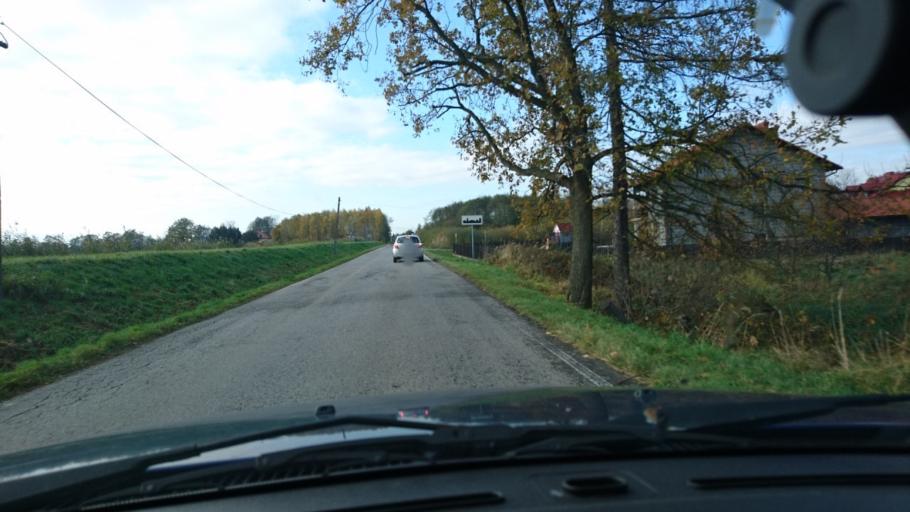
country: PL
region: Lesser Poland Voivodeship
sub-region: Powiat oswiecimski
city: Malec
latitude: 49.9411
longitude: 19.2232
